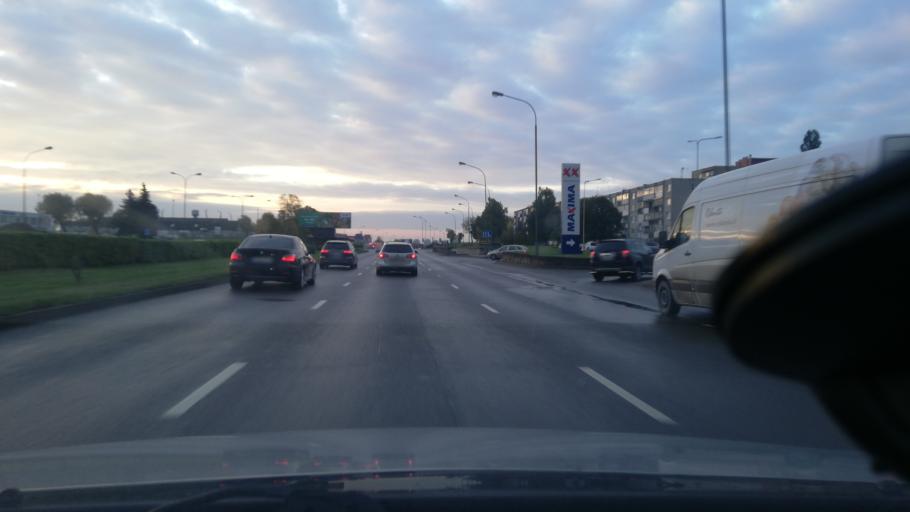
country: LT
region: Klaipedos apskritis
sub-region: Klaipeda
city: Klaipeda
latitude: 55.6897
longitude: 21.1804
